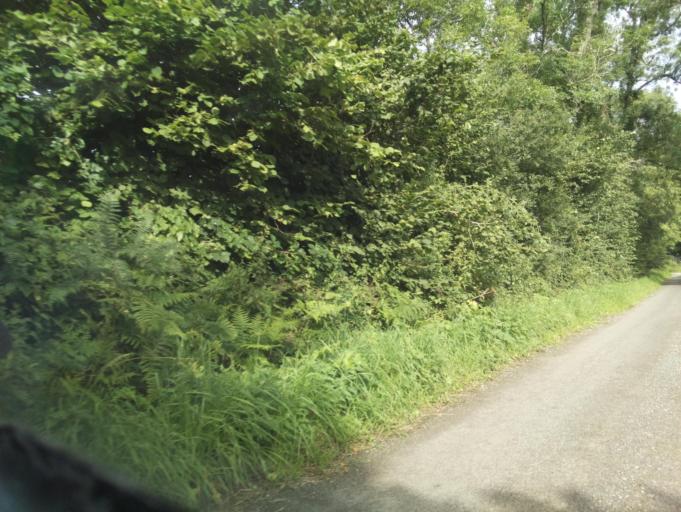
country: GB
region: England
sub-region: Somerset
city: Chilcompton
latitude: 51.2545
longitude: -2.5516
